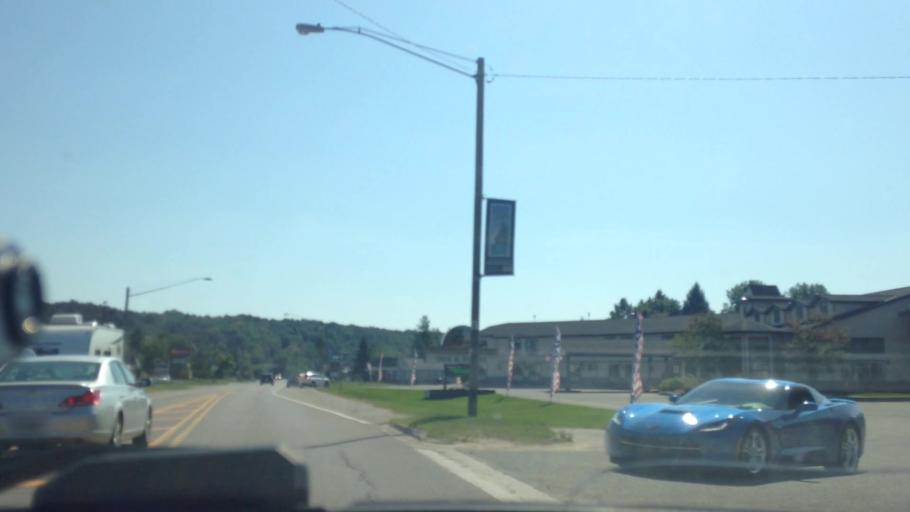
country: US
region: Michigan
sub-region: Alger County
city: Munising
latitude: 46.4071
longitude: -86.6510
